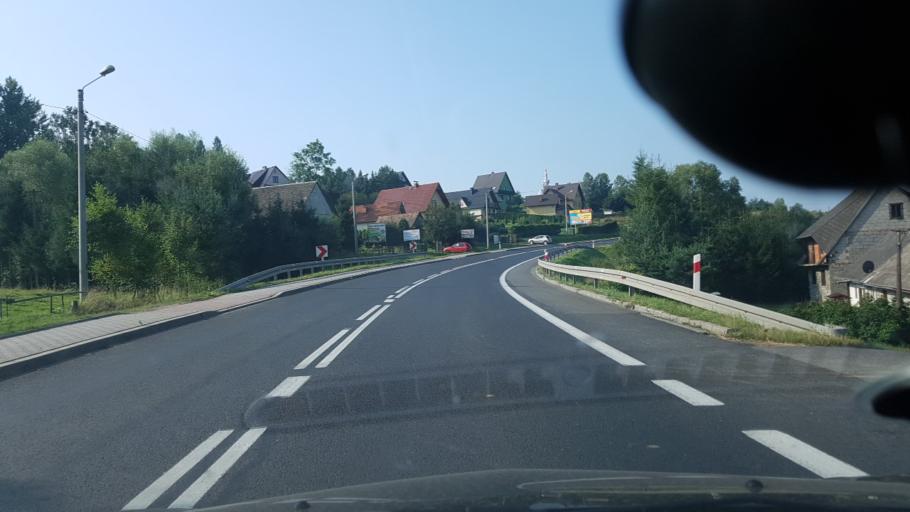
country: PL
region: Lesser Poland Voivodeship
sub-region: Powiat nowotarski
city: Jablonka
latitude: 49.4895
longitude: 19.7041
